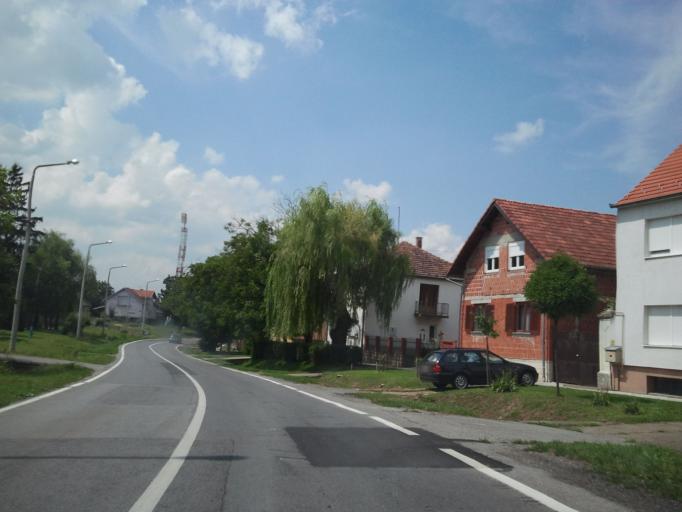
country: HR
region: Vukovarsko-Srijemska
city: Lovas
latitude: 45.2951
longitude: 19.0982
